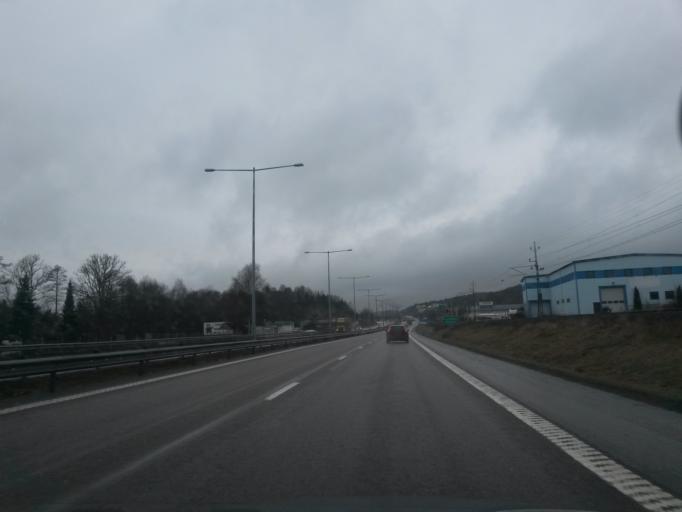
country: SE
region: Vaestra Goetaland
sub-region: Uddevalla Kommun
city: Uddevalla
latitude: 58.3524
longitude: 11.9732
